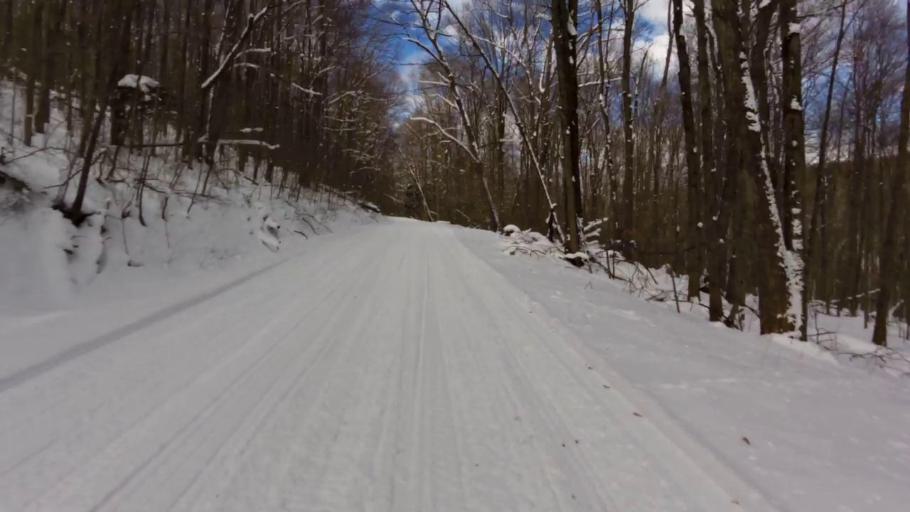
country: US
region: Pennsylvania
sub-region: McKean County
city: Bradford
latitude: 42.0341
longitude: -78.7032
